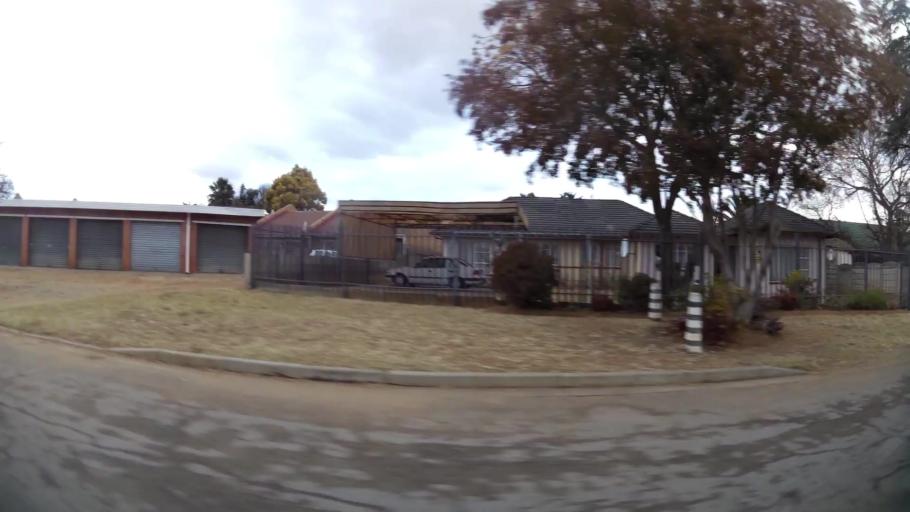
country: ZA
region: Orange Free State
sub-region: Lejweleputswa District Municipality
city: Welkom
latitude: -27.9646
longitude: 26.7252
